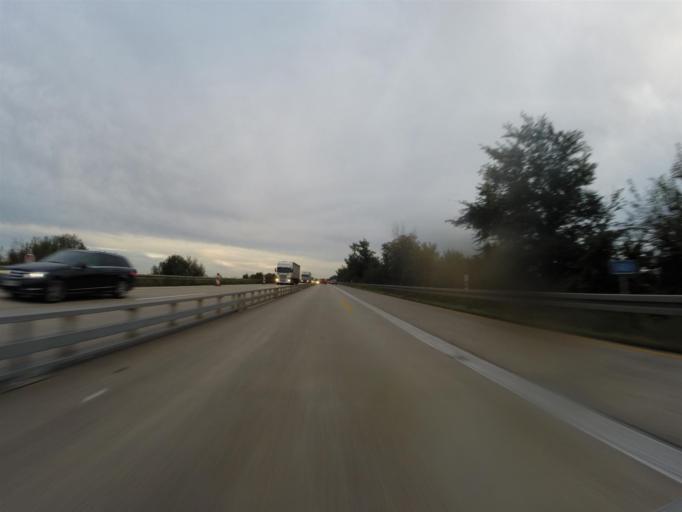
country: DE
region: Saxony-Anhalt
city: Osterfeld
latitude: 51.0874
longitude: 11.9555
